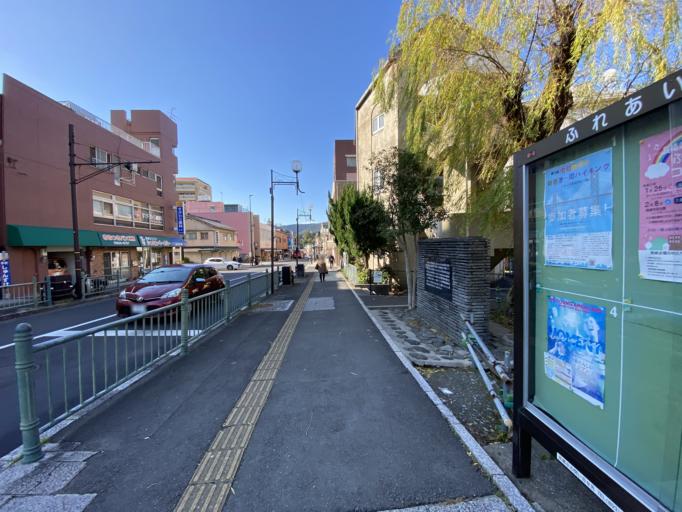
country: JP
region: Nagasaki
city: Nagasaki-shi
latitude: 32.7761
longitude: 129.8669
